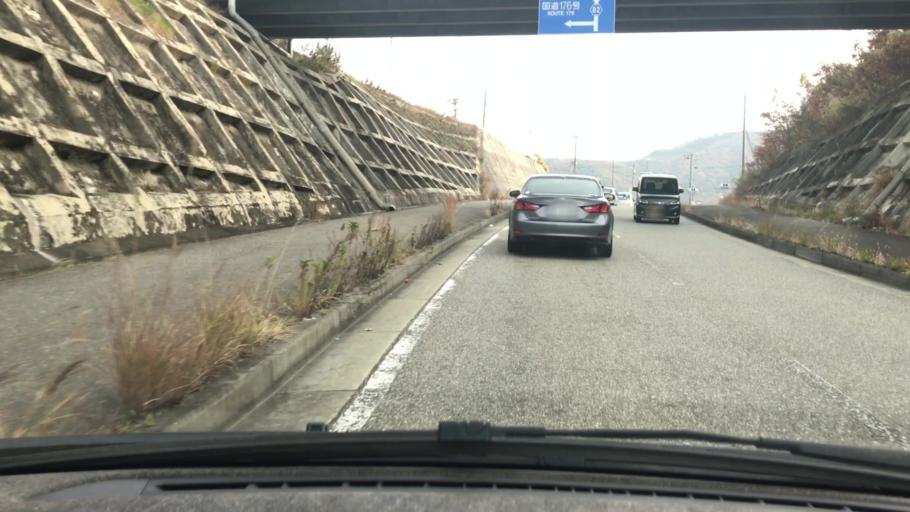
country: JP
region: Hyogo
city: Sandacho
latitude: 34.8215
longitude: 135.2505
